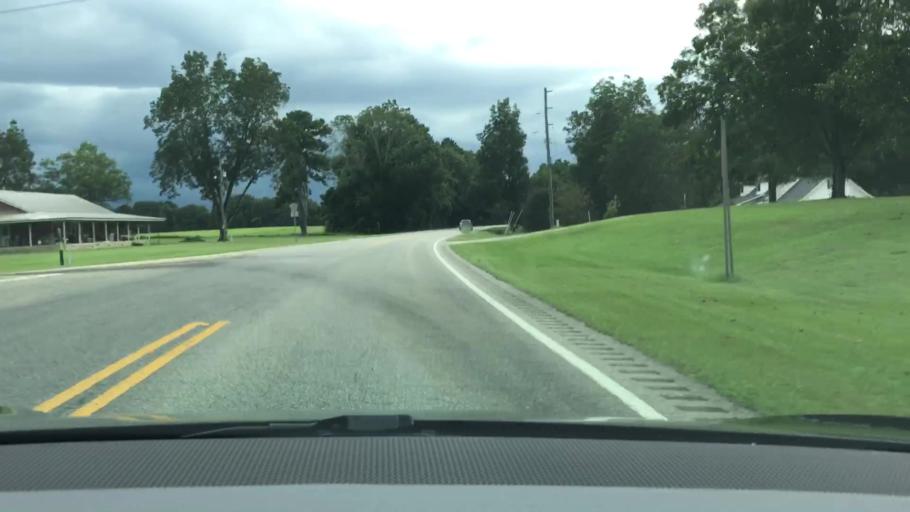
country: US
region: Alabama
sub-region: Coffee County
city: Elba
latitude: 31.5245
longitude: -86.0375
